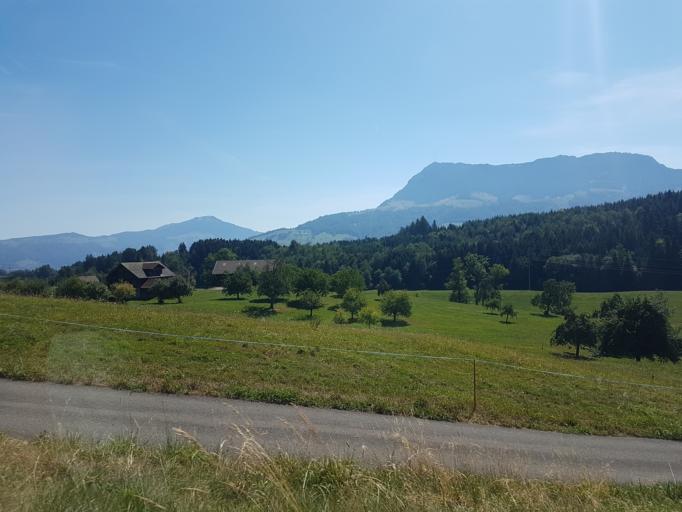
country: CH
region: Lucerne
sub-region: Lucerne-Land District
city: Udligenswil
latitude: 47.0854
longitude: 8.3996
